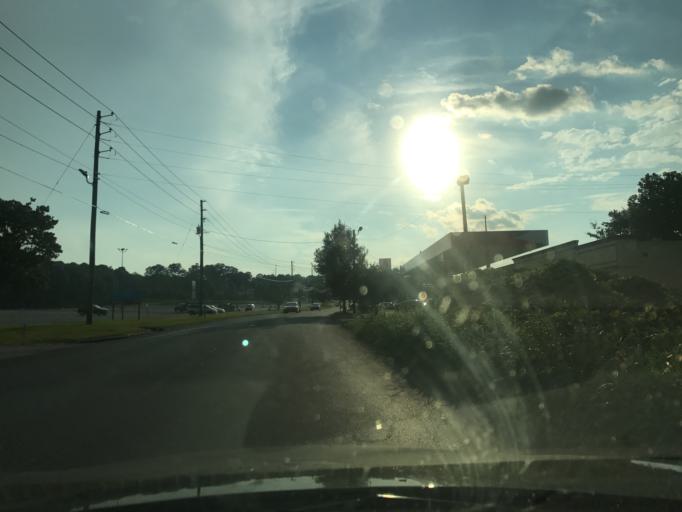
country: US
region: Georgia
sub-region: DeKalb County
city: Gresham Park
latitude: 33.7159
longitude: -84.3458
